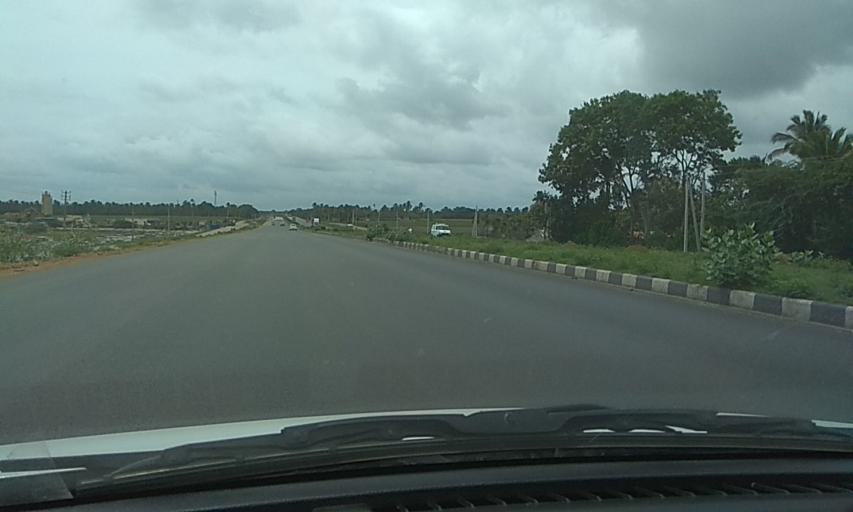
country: IN
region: Karnataka
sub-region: Davanagere
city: Mayakonda
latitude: 14.3534
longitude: 76.2008
